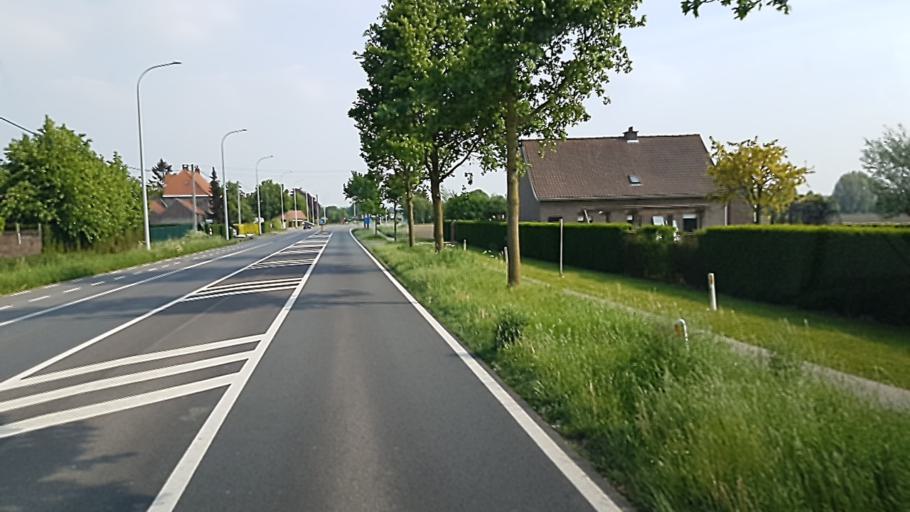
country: BE
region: Wallonia
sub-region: Province du Hainaut
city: Pecq
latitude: 50.7401
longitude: 3.3265
